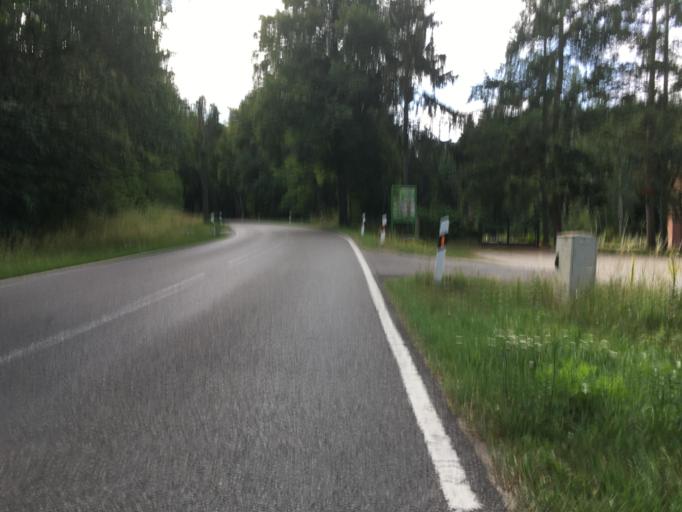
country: DE
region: Brandenburg
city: Friedrichswalde
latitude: 53.0539
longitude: 13.7147
